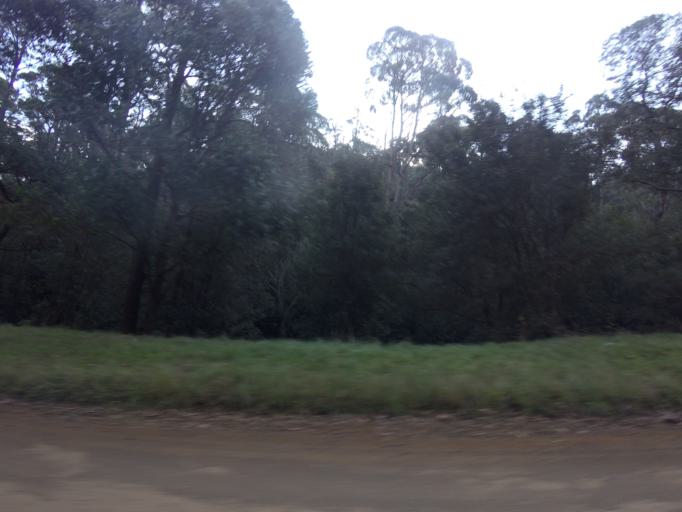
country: AU
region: Tasmania
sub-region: Sorell
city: Sorell
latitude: -42.4849
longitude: 147.4395
